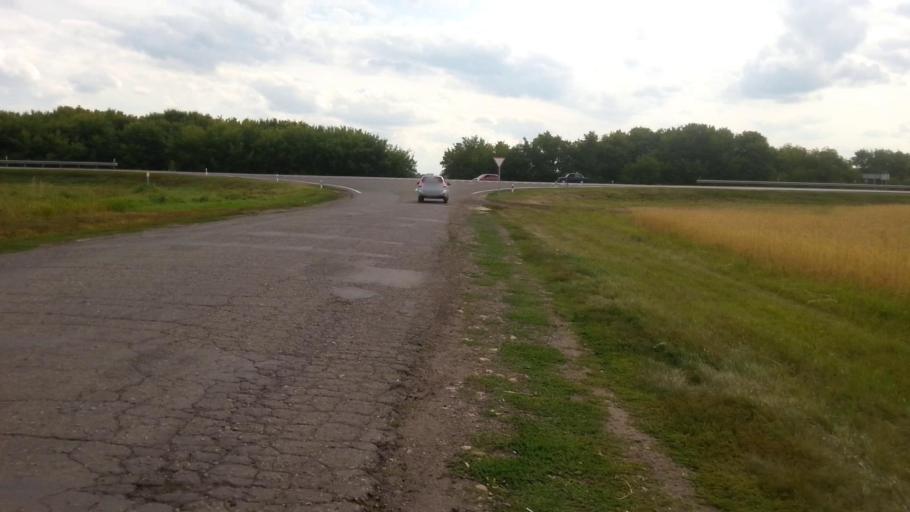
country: RU
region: Altai Krai
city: Nauchnyy Gorodok
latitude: 53.3575
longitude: 83.5082
